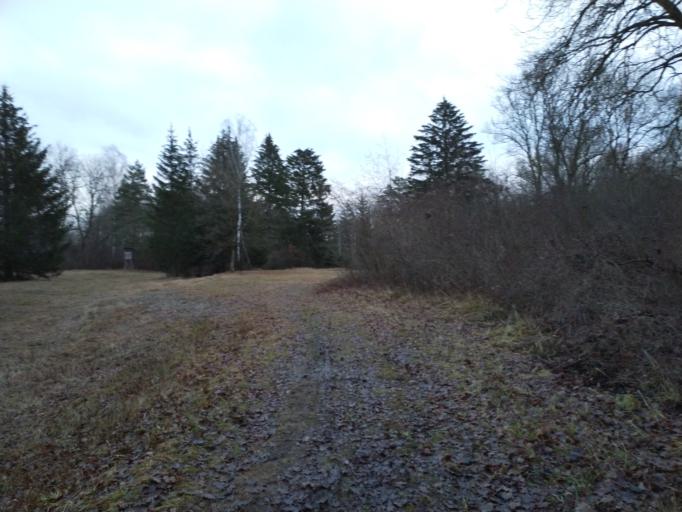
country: DE
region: Bavaria
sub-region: Swabia
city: Guenzburg
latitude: 48.4764
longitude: 10.3087
